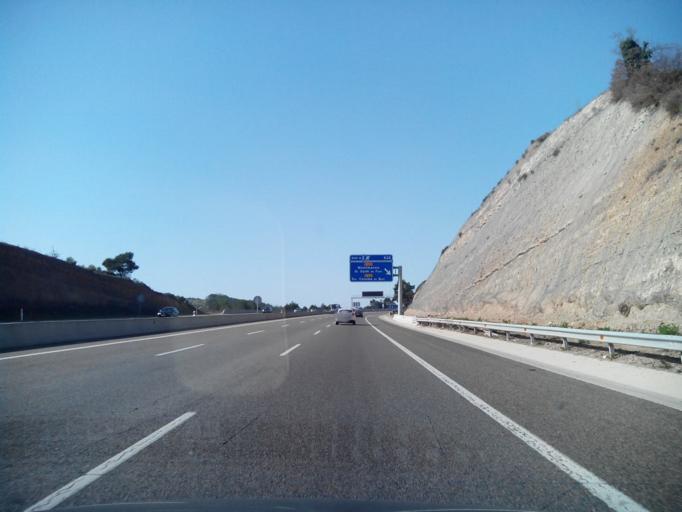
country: ES
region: Catalonia
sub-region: Provincia de Lleida
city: Sant Guim de Freixenet
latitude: 41.6247
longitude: 1.4214
